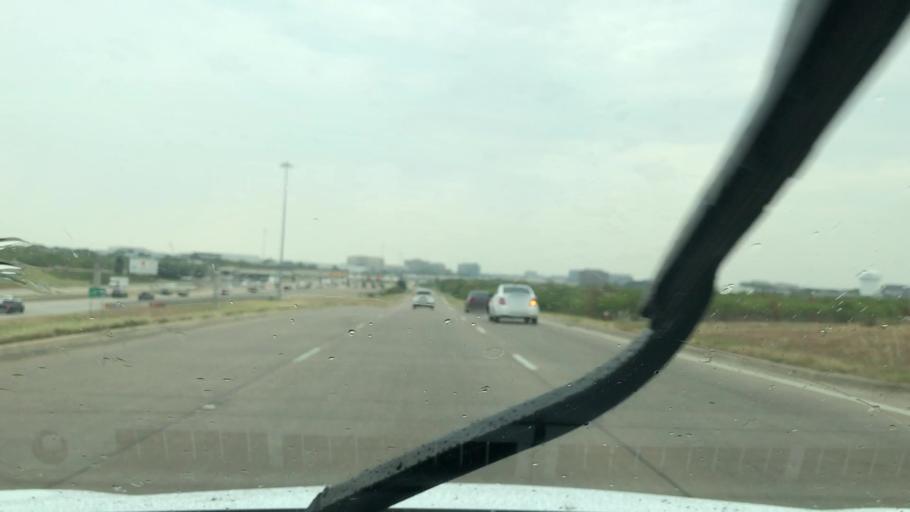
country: US
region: Texas
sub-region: Dallas County
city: Irving
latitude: 32.8782
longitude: -96.9901
